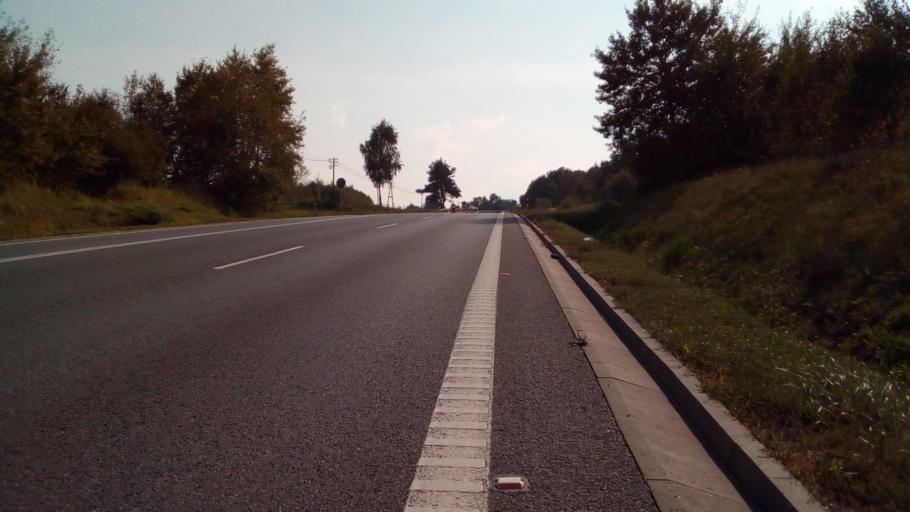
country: PL
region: Subcarpathian Voivodeship
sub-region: Powiat strzyzowski
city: Jawornik
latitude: 49.8407
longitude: 21.8891
